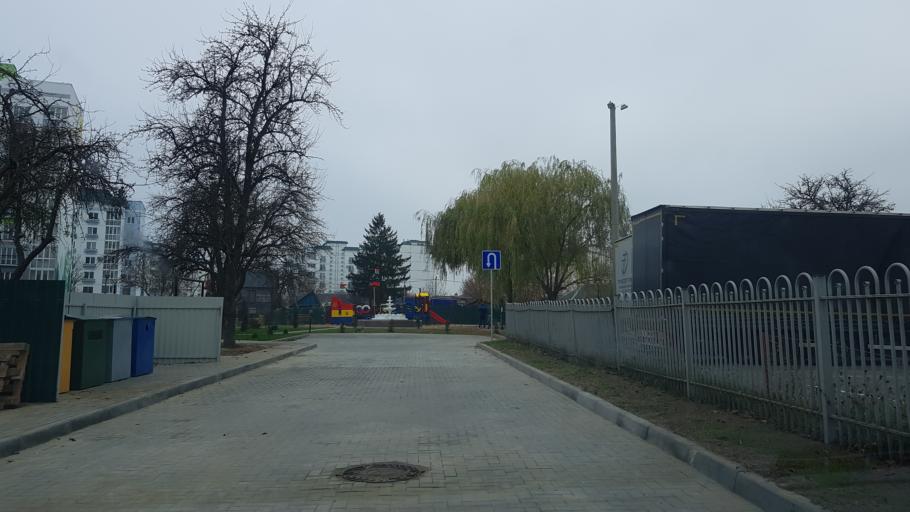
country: BY
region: Mogilev
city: Babruysk
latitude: 53.1537
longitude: 29.2463
